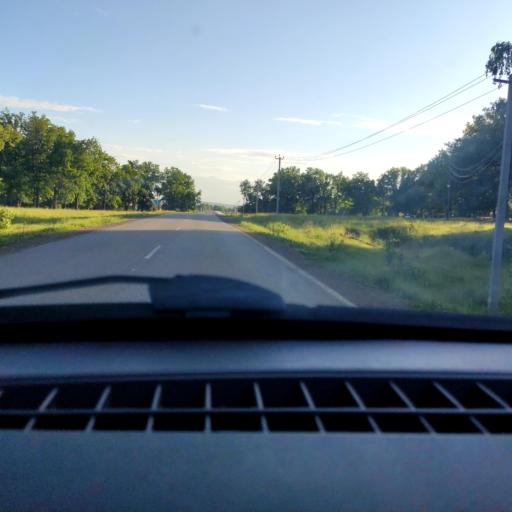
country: RU
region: Bashkortostan
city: Avdon
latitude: 54.6230
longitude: 55.6793
